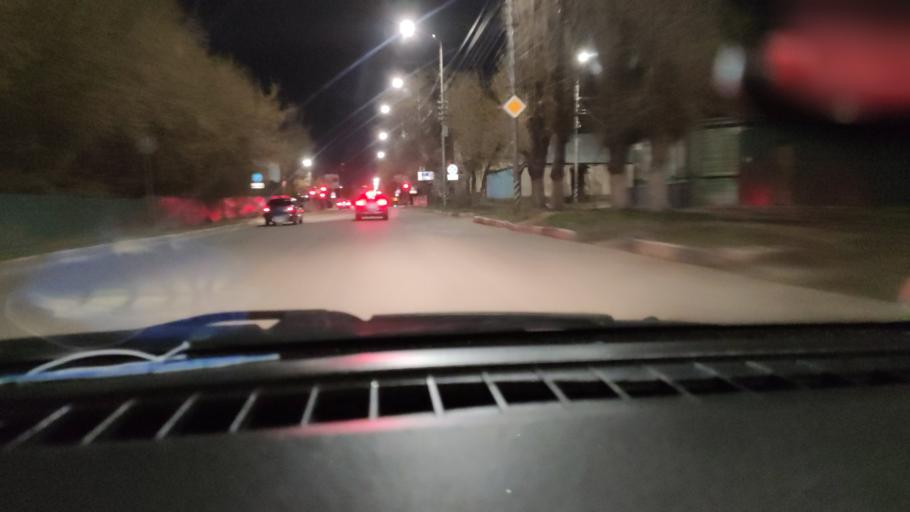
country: RU
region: Saratov
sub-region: Saratovskiy Rayon
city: Saratov
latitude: 51.5416
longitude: 46.0436
